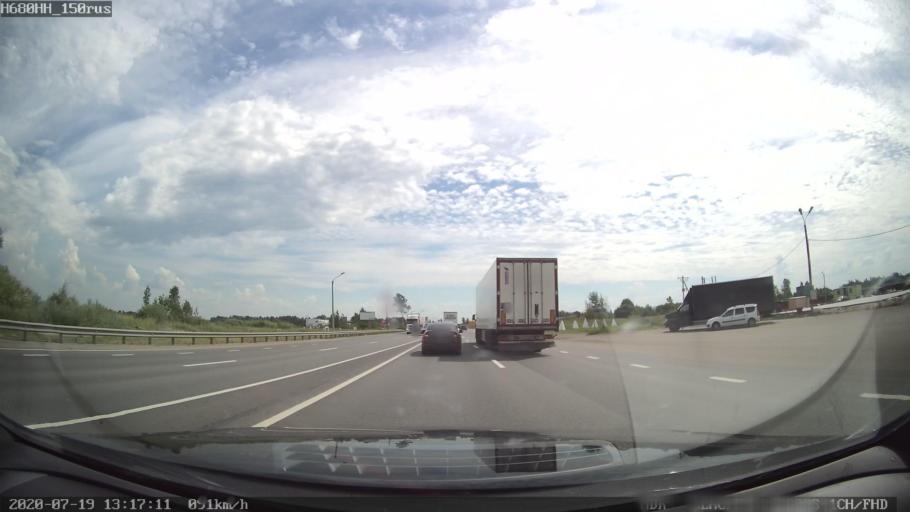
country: RU
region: St.-Petersburg
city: Kolpino
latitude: 59.7107
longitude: 30.5666
